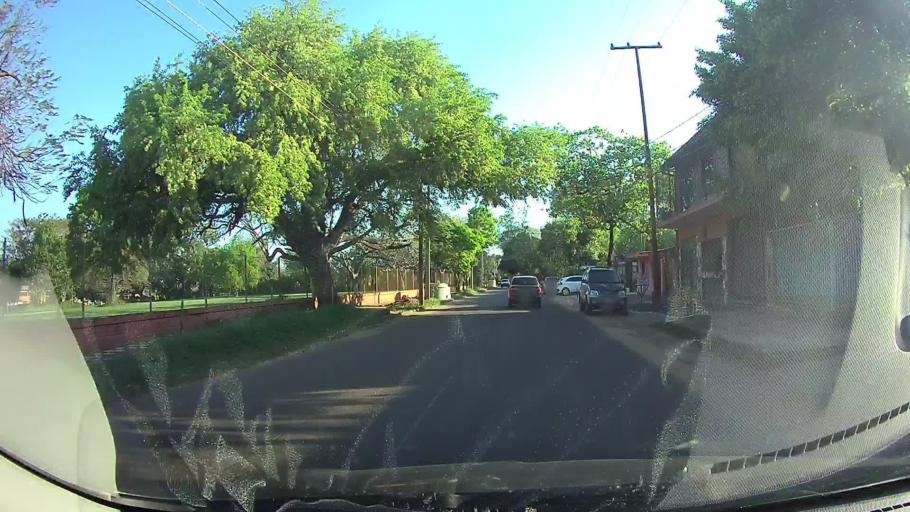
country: PY
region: Central
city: Fernando de la Mora
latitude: -25.3427
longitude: -57.5322
